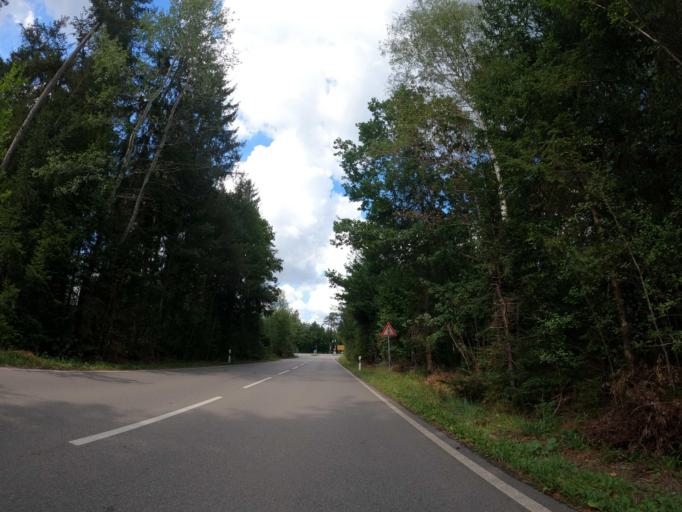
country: DE
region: Bavaria
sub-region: Upper Bavaria
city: Ottobrunn
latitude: 48.0436
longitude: 11.6701
